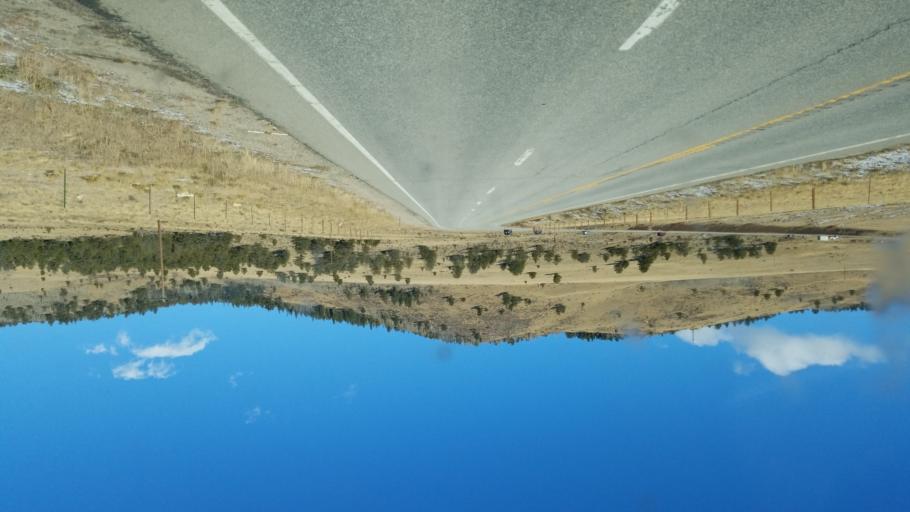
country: US
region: Colorado
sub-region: Park County
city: Fairplay
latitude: 39.2765
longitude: -105.9480
